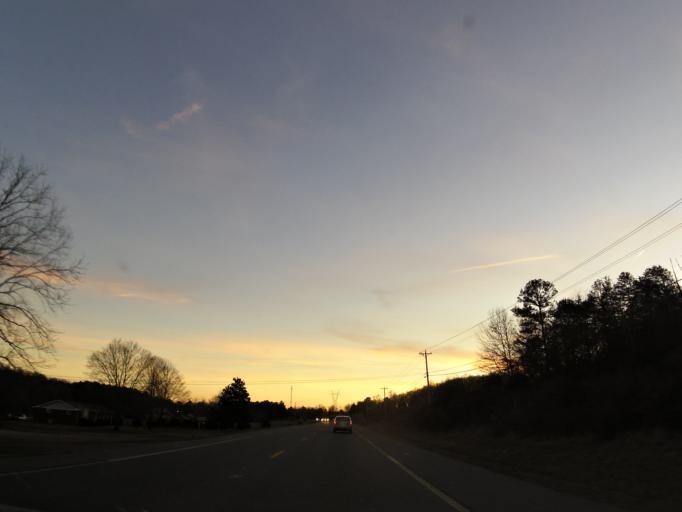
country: US
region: Tennessee
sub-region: Bradley County
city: Wildwood Lake
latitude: 35.0795
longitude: -84.8905
